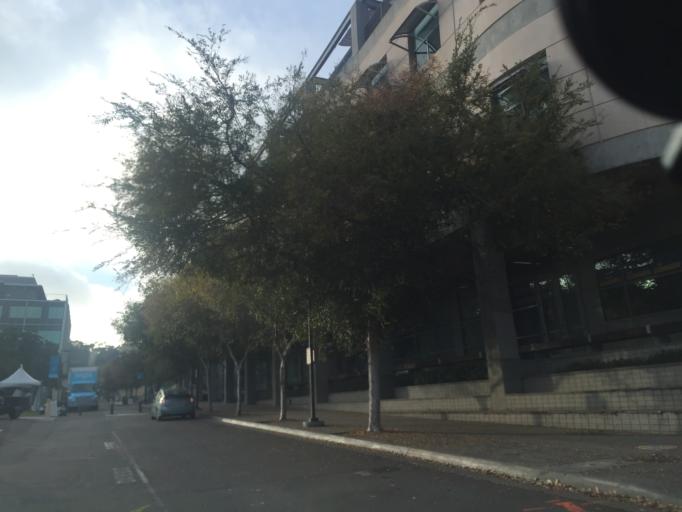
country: US
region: California
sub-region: San Diego County
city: La Jolla
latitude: 32.8794
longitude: -117.2346
